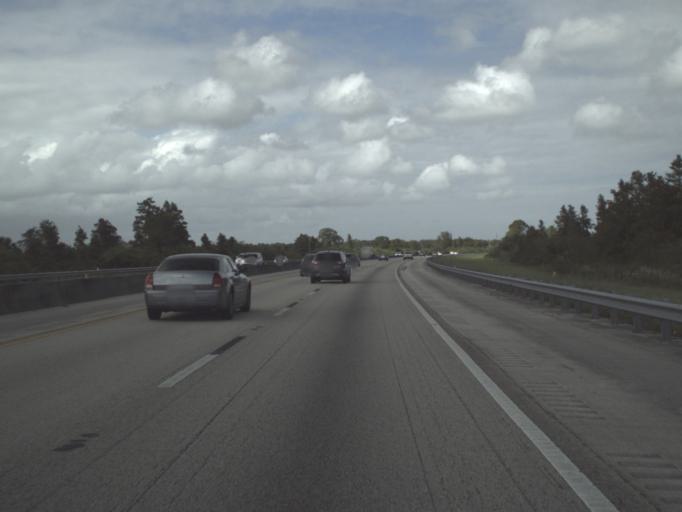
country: US
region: Florida
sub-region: Martin County
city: Hobe Sound
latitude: 27.0351
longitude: -80.2381
